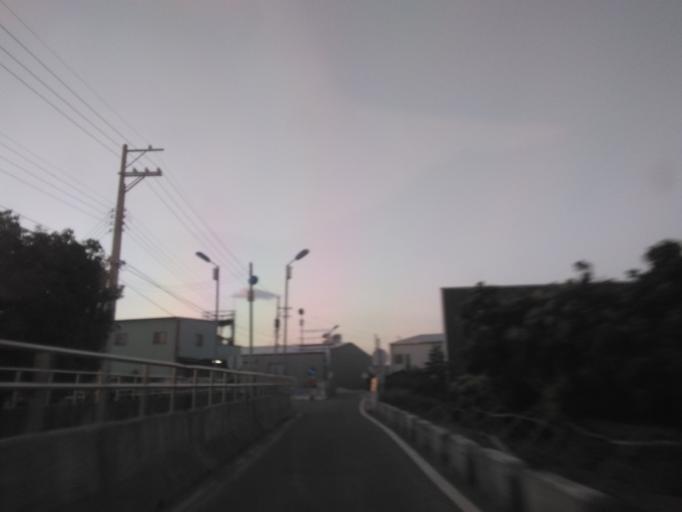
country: TW
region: Taiwan
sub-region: Changhua
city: Chang-hua
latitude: 24.0874
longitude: 120.5926
